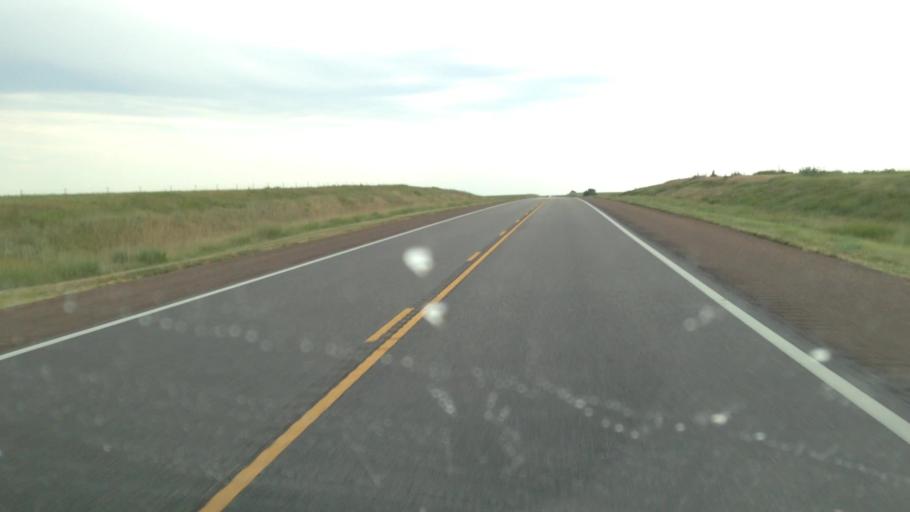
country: US
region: Kansas
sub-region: Coffey County
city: Burlington
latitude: 38.0587
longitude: -95.7391
